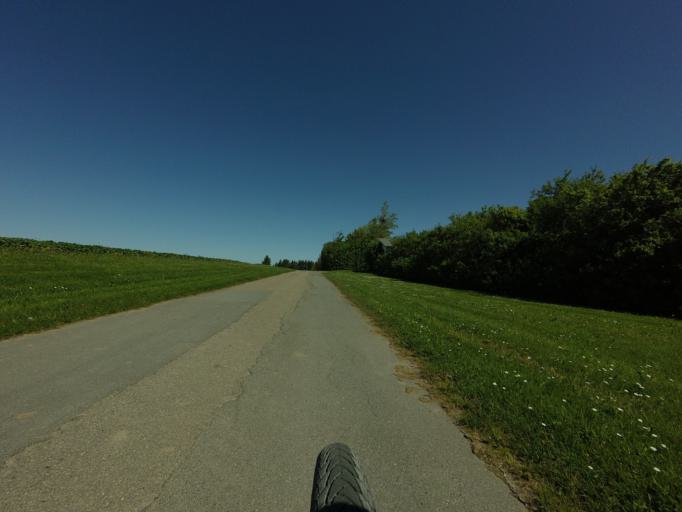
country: DK
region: North Denmark
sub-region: Hjorring Kommune
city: Hjorring
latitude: 57.4556
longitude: 9.8956
